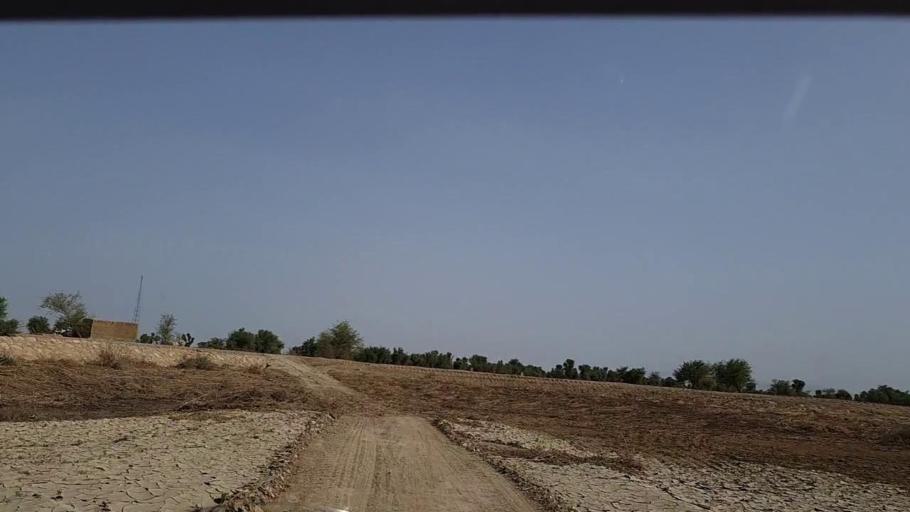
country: PK
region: Sindh
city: Johi
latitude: 26.6414
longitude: 67.5026
